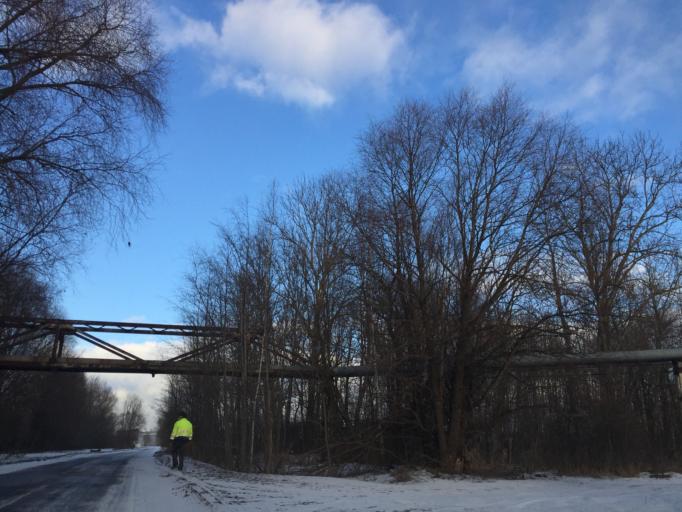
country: LV
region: Riga
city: Riga
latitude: 56.9847
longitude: 24.1098
